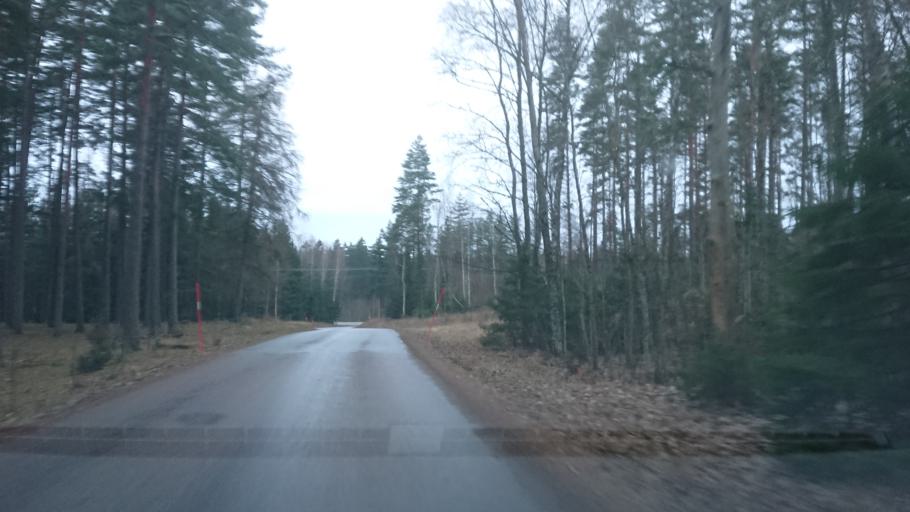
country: SE
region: Uppsala
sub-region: Osthammars Kommun
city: Bjorklinge
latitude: 60.0175
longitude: 17.5805
